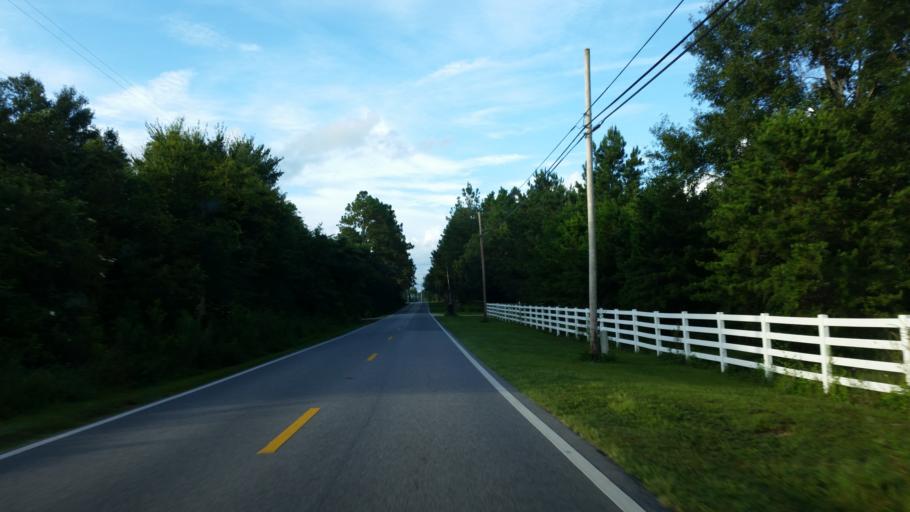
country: US
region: Florida
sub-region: Escambia County
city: Bellview
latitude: 30.5029
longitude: -87.3312
